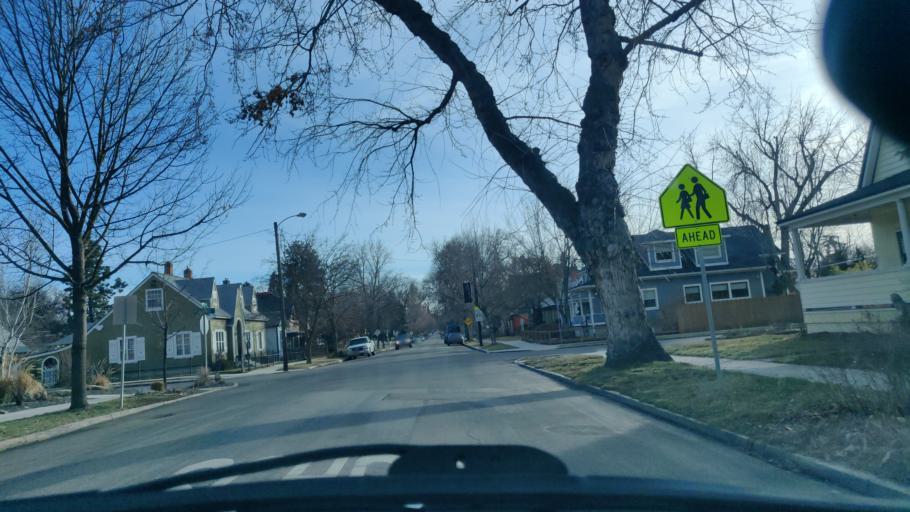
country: US
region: Idaho
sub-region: Ada County
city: Boise
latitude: 43.6296
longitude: -116.1987
